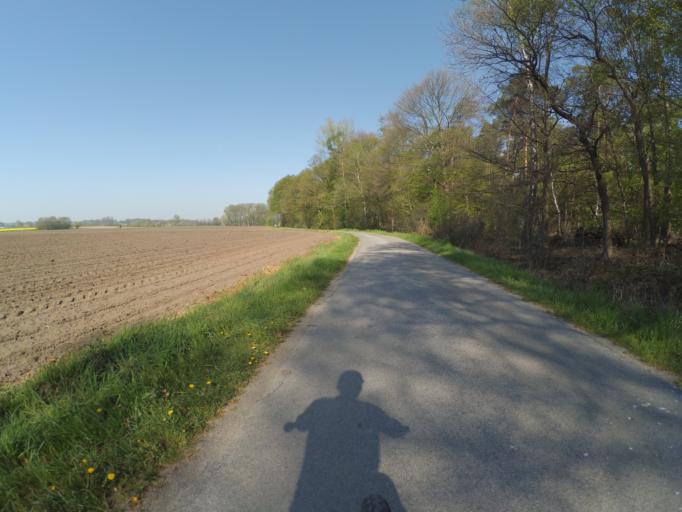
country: DE
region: North Rhine-Westphalia
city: Ludinghausen
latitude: 51.7919
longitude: 7.4175
